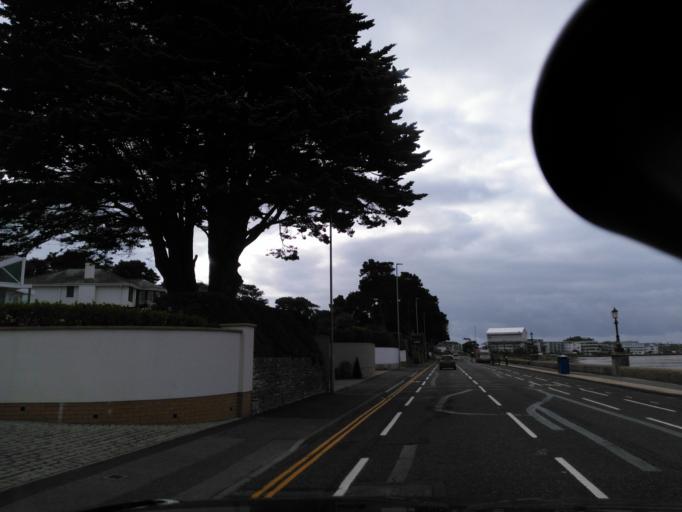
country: GB
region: England
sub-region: Dorset
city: Parkstone
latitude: 50.6998
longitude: -1.9344
